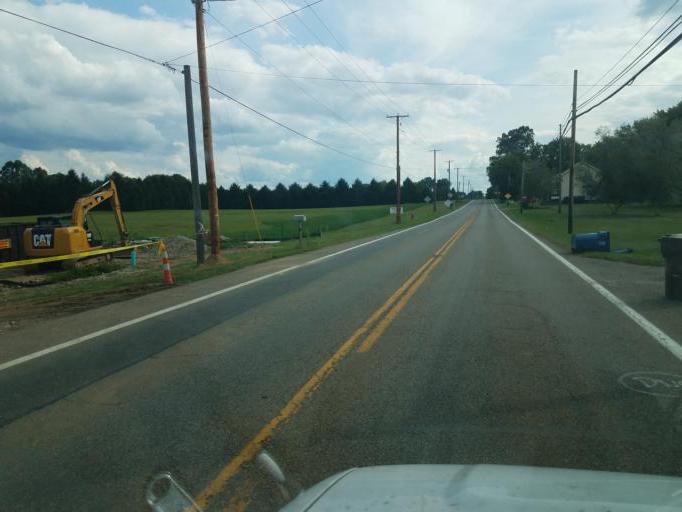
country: US
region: Ohio
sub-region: Stark County
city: Louisville
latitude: 40.8558
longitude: -81.2587
